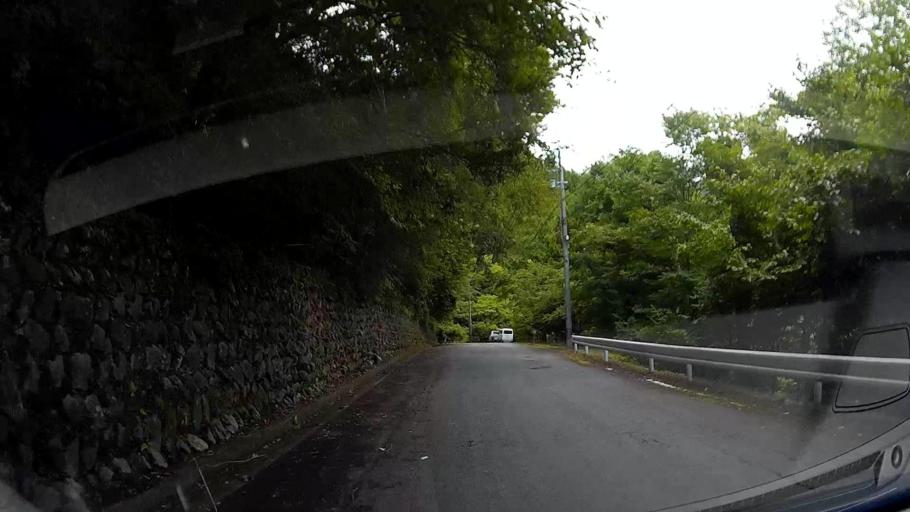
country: JP
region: Shizuoka
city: Shizuoka-shi
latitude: 35.3122
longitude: 138.1867
